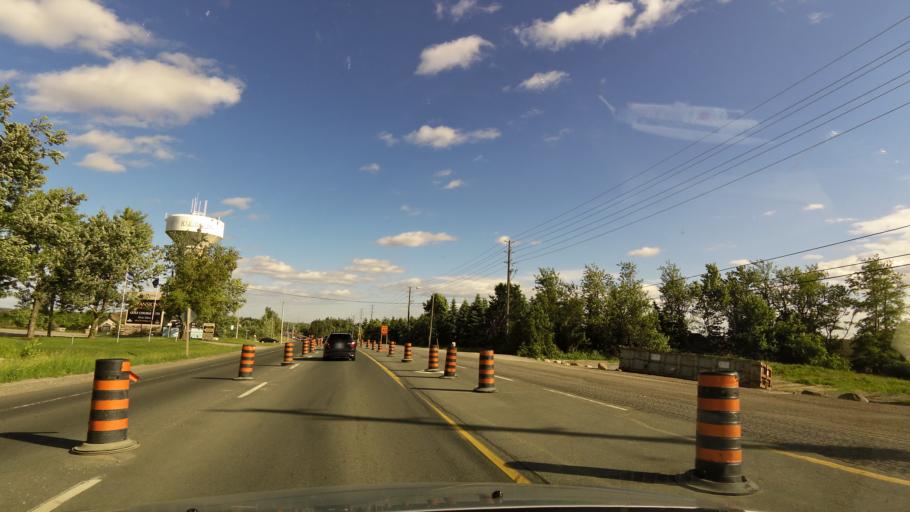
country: CA
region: Ontario
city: Vaughan
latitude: 43.8534
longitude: -79.6404
